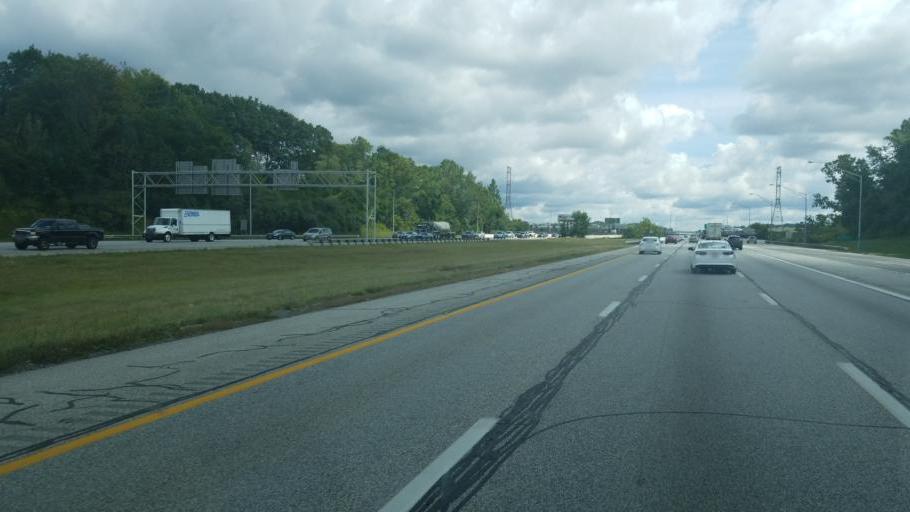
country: US
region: Ohio
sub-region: Cuyahoga County
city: Garfield Heights
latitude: 41.4072
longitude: -81.6398
